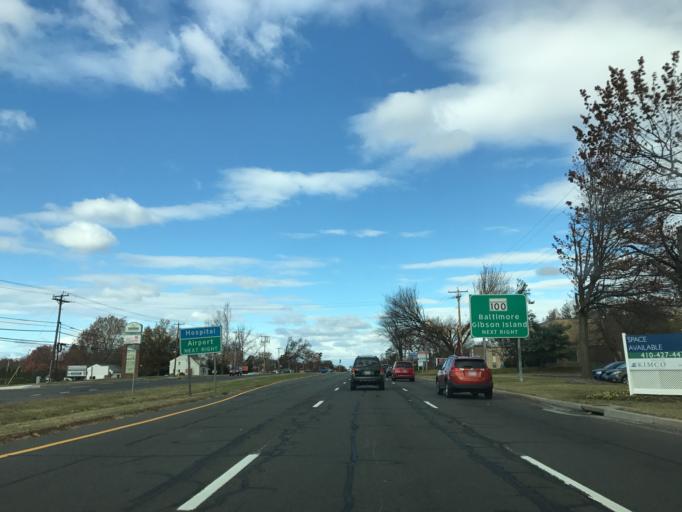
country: US
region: Maryland
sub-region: Anne Arundel County
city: Pasadena
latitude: 39.1284
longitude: -76.5916
